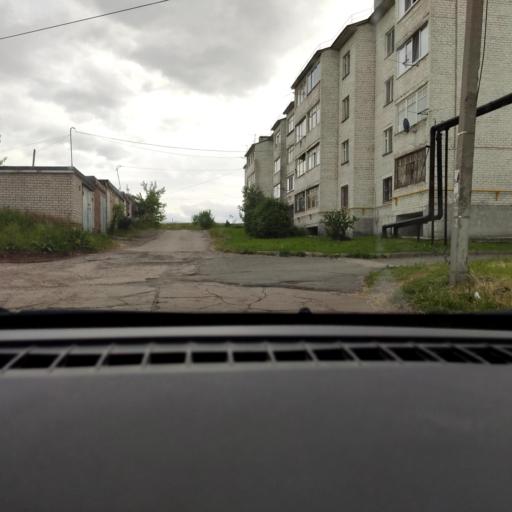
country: RU
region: Perm
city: Lobanovo
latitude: 57.8604
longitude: 56.2945
